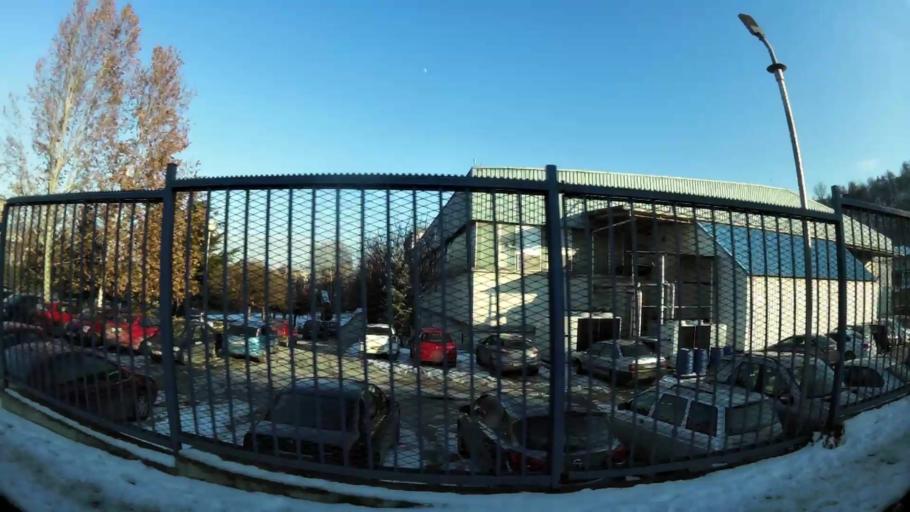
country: MK
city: Krushopek
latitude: 41.9992
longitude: 21.3810
